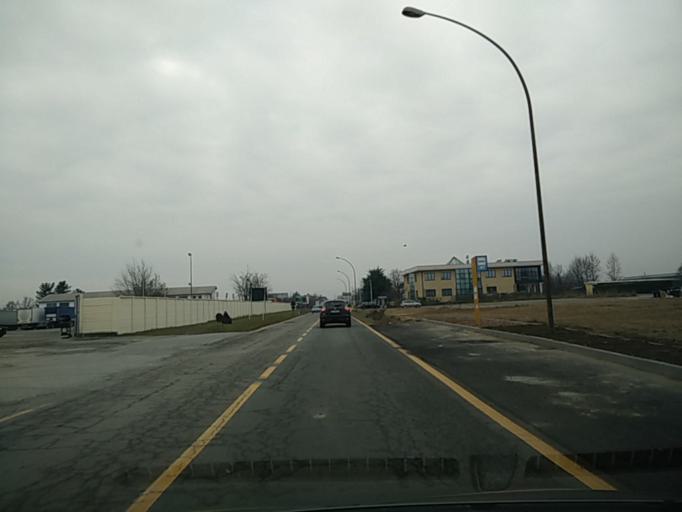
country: IT
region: Piedmont
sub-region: Provincia di Torino
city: Leini
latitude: 45.2021
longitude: 7.7259
